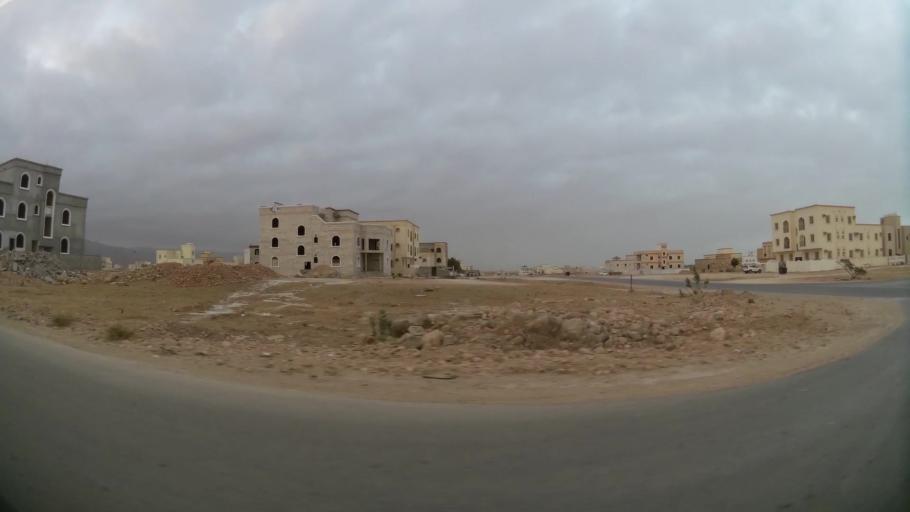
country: OM
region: Zufar
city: Salalah
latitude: 17.0428
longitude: 54.0373
